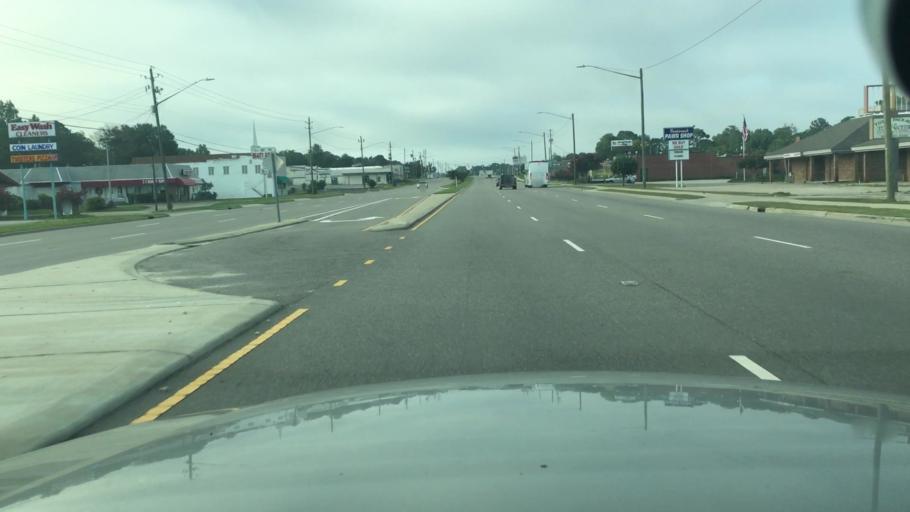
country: US
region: North Carolina
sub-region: Cumberland County
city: Fort Bragg
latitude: 35.0971
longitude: -78.9566
